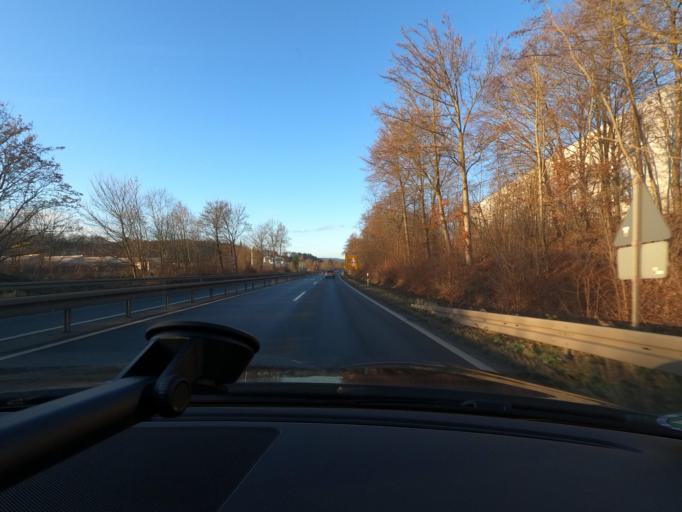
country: DE
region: Lower Saxony
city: Badenhausen
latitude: 51.7536
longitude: 10.2166
